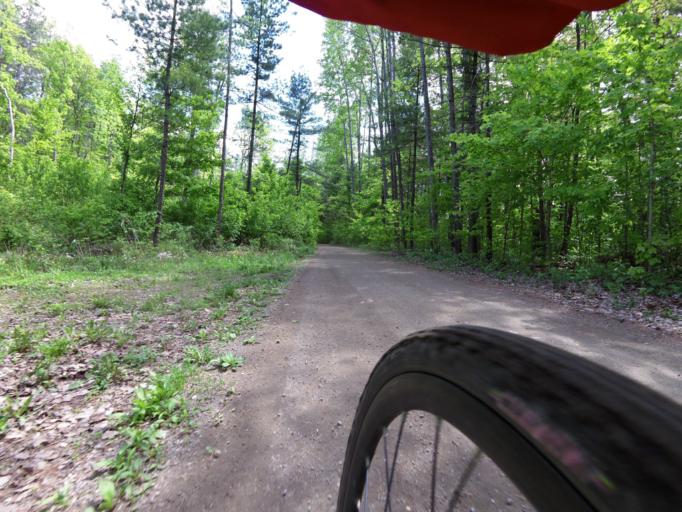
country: CA
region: Ontario
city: Renfrew
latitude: 45.2105
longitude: -76.6922
